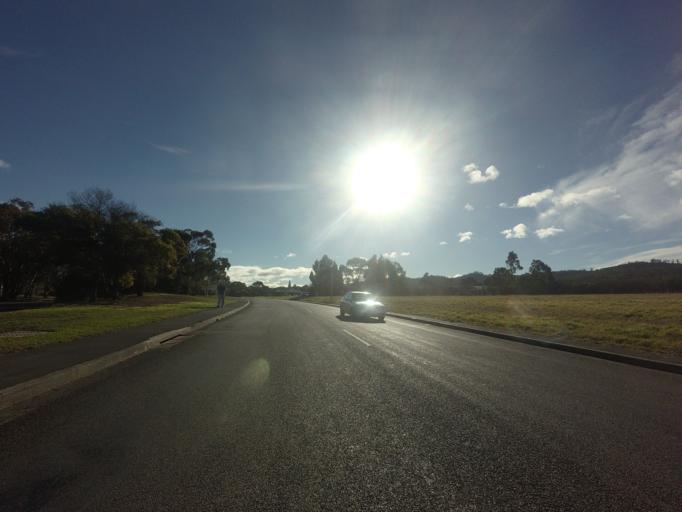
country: AU
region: Tasmania
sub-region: Clarence
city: Rokeby
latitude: -42.8963
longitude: 147.4467
